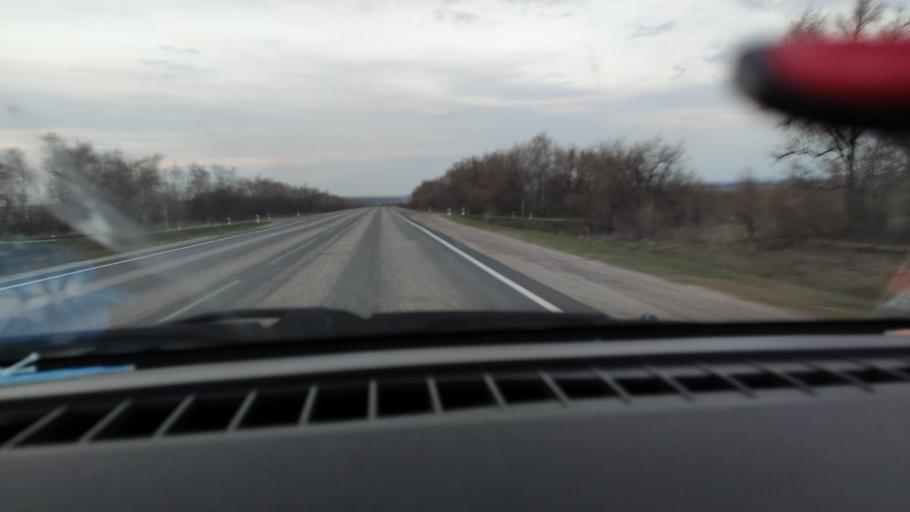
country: RU
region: Saratov
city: Sinodskoye
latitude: 51.9532
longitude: 46.6112
